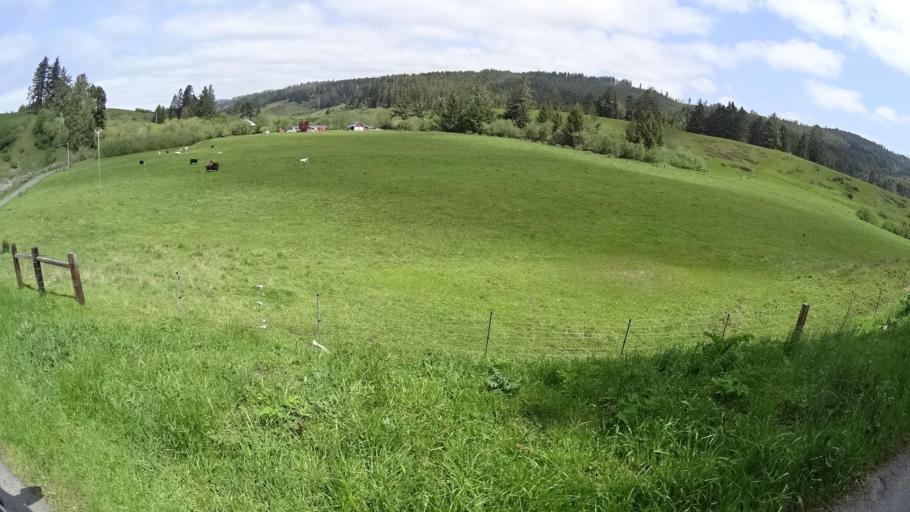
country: US
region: California
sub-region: Humboldt County
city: Fortuna
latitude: 40.6428
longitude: -124.1893
